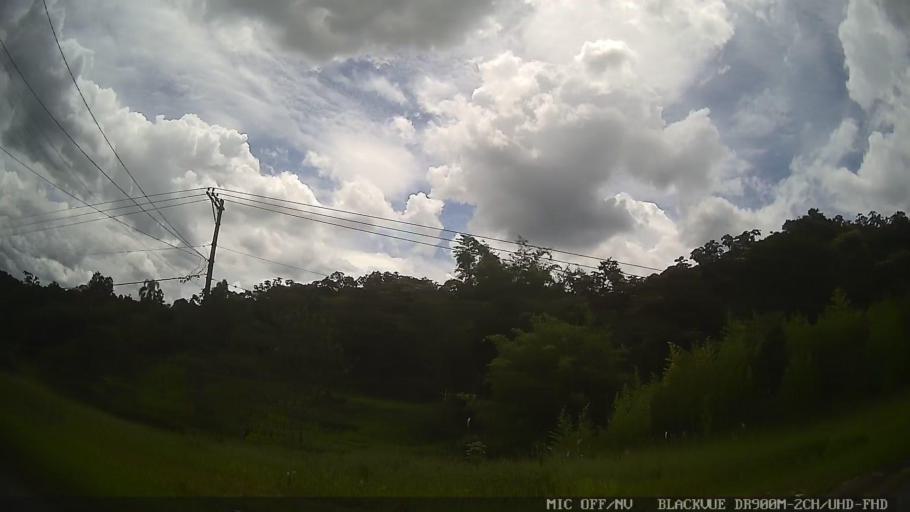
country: BR
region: Sao Paulo
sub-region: Suzano
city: Suzano
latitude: -23.6065
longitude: -46.3115
